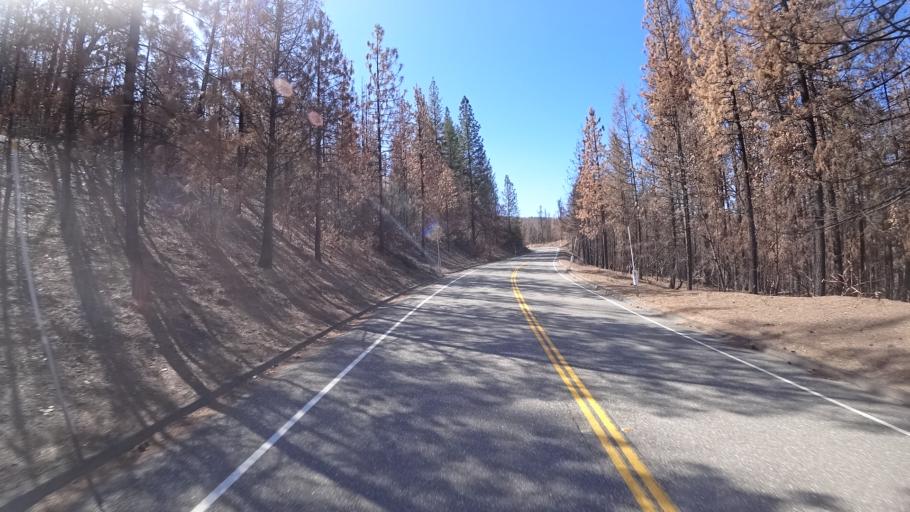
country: US
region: California
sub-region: Tehama County
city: Rancho Tehama Reserve
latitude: 39.6741
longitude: -122.7112
